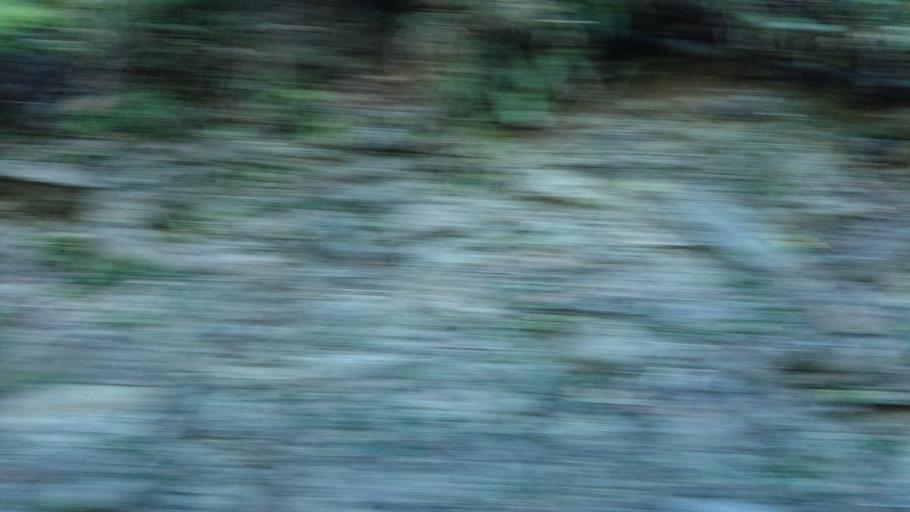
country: TW
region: Taiwan
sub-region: Hualien
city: Hualian
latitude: 24.3511
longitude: 121.3249
